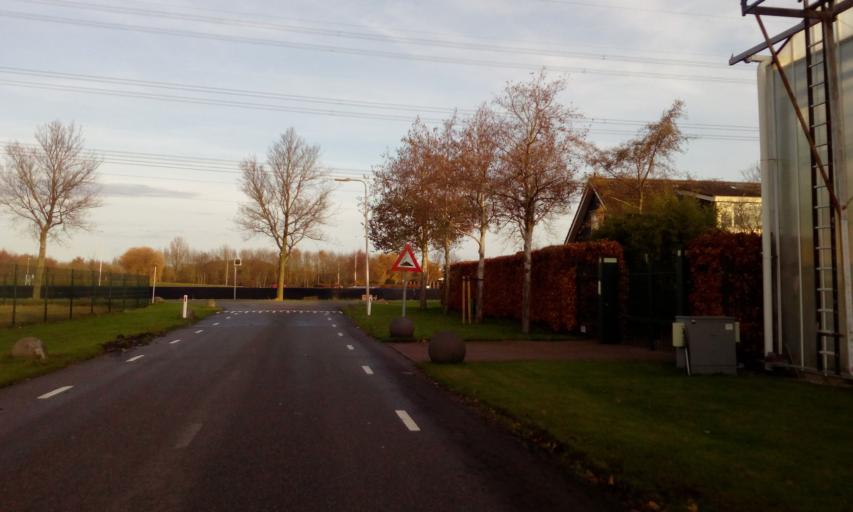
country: NL
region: South Holland
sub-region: Gemeente Zoetermeer
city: Zoetermeer
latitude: 52.0305
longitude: 4.4867
